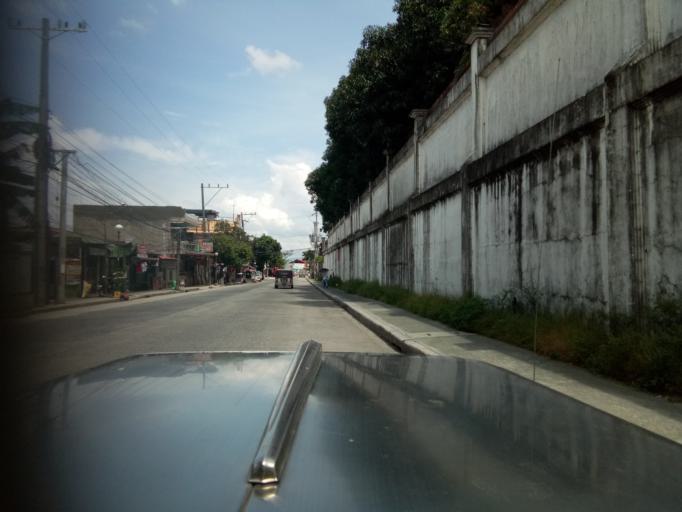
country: PH
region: Calabarzon
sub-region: Province of Cavite
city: Bulihan
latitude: 14.2852
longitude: 120.9970
